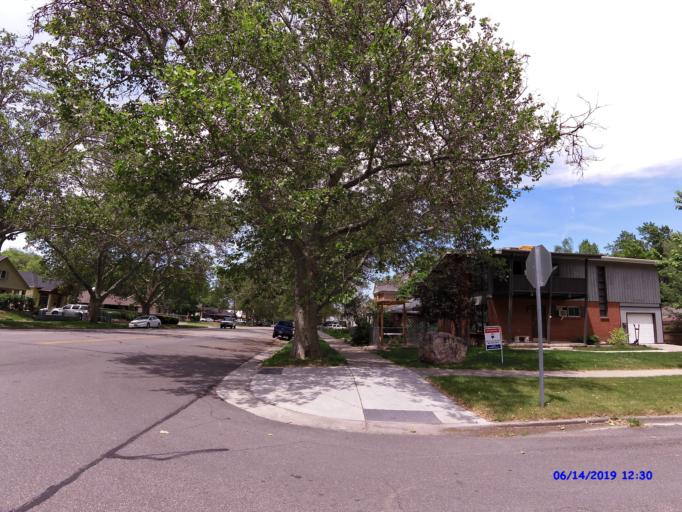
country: US
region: Utah
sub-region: Weber County
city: Ogden
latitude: 41.2226
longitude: -111.9510
